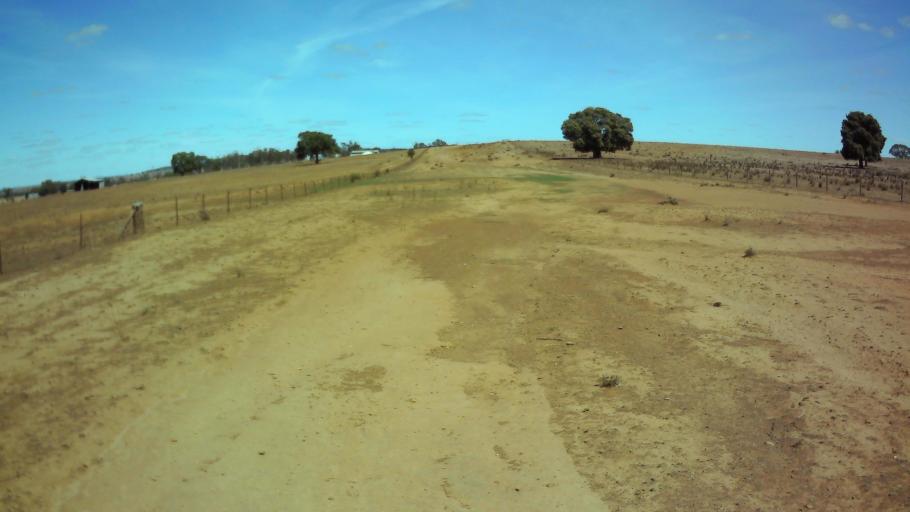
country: AU
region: New South Wales
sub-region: Forbes
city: Forbes
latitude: -33.7178
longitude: 147.8176
